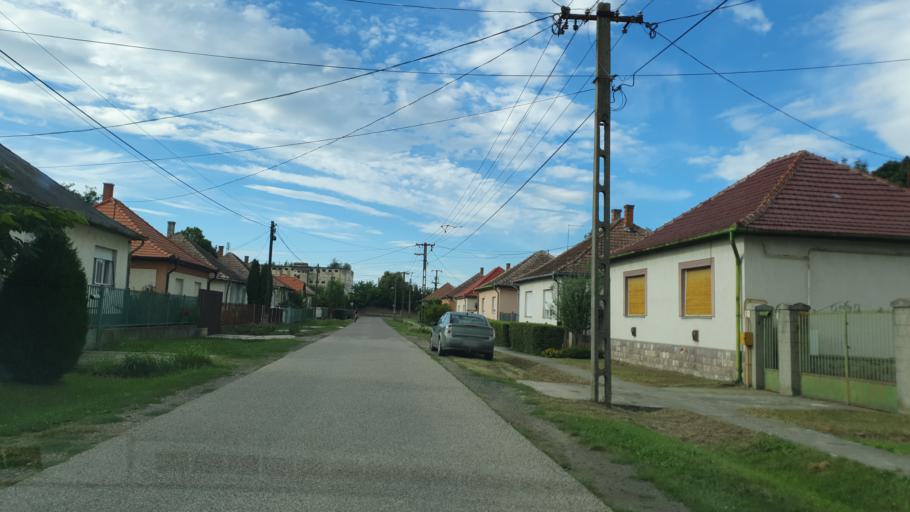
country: HU
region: Heves
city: Zagyvaszanto
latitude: 47.7613
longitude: 19.6777
